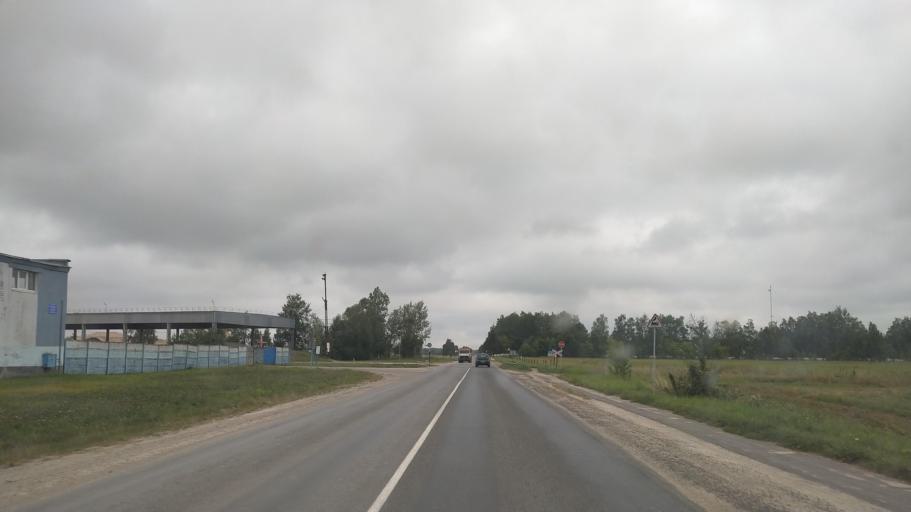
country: BY
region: Brest
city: Byaroza
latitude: 52.5522
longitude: 24.9335
